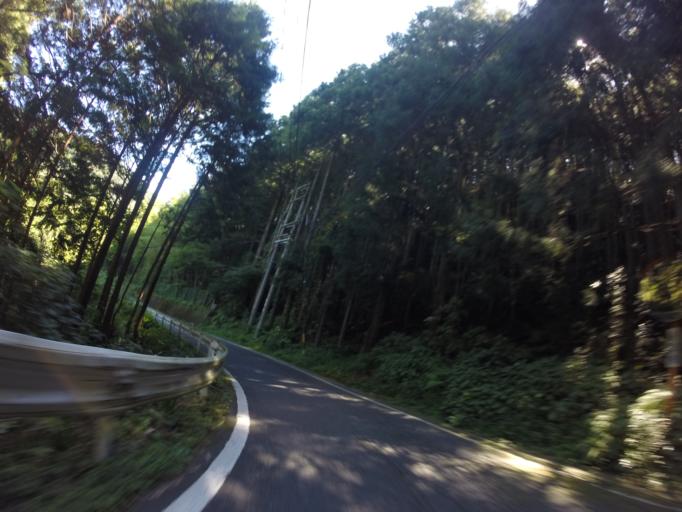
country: JP
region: Shizuoka
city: Fujieda
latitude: 34.9732
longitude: 138.2093
